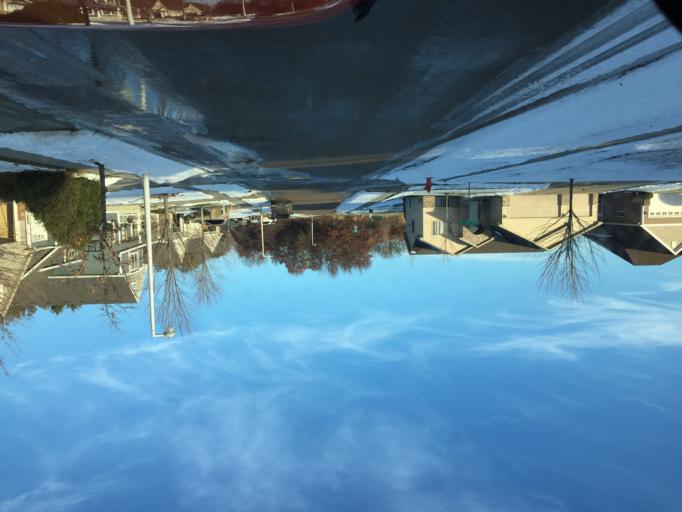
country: US
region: Minnesota
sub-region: Olmsted County
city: Rochester
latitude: 44.0363
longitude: -92.4245
